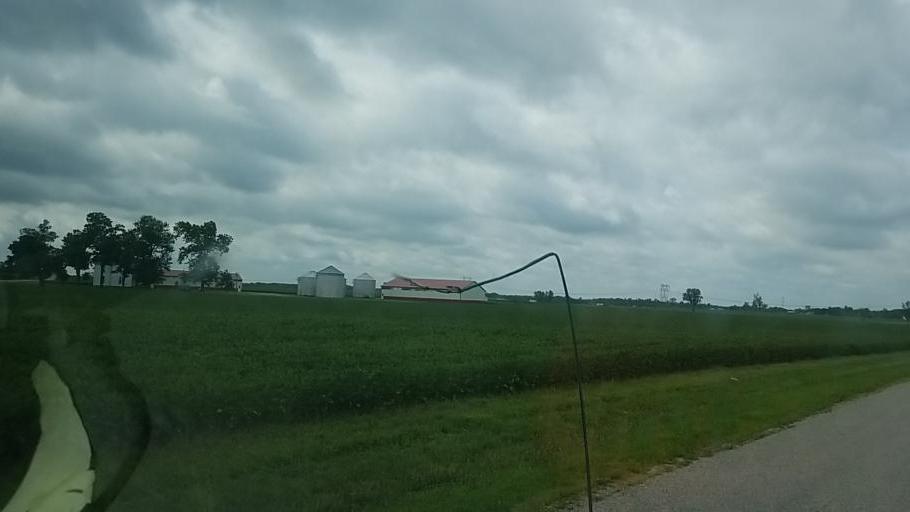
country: US
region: Ohio
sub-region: Madison County
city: Mount Sterling
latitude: 39.7995
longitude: -83.2313
